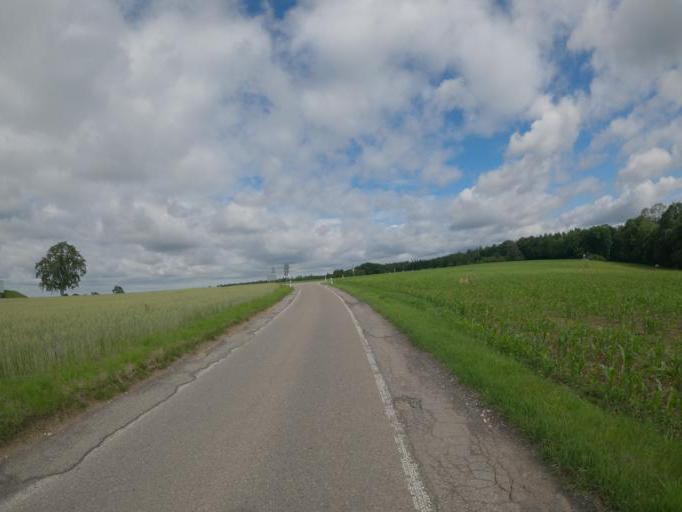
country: DE
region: Baden-Wuerttemberg
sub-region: Regierungsbezirk Stuttgart
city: Ebersbach an der Fils
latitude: 48.7349
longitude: 9.5329
